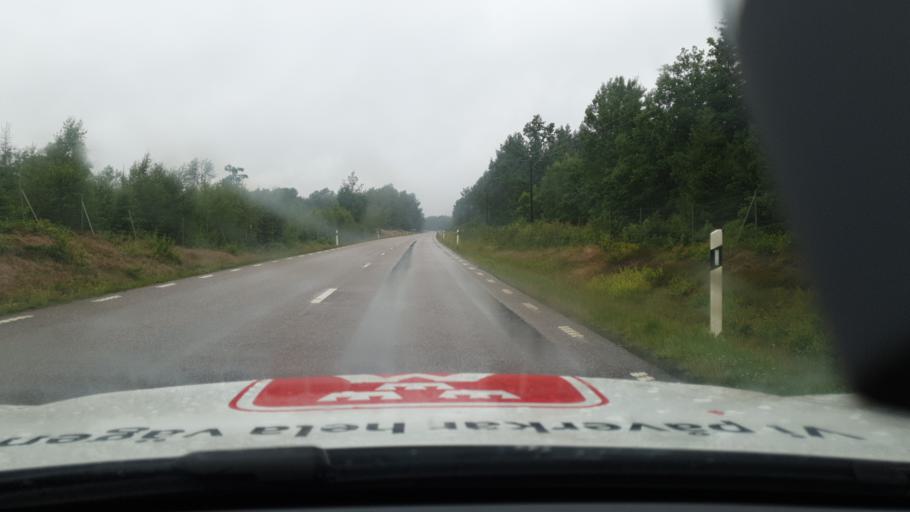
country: SE
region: Vaestra Goetaland
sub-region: Falkopings Kommun
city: Floby
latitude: 58.1844
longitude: 13.3630
